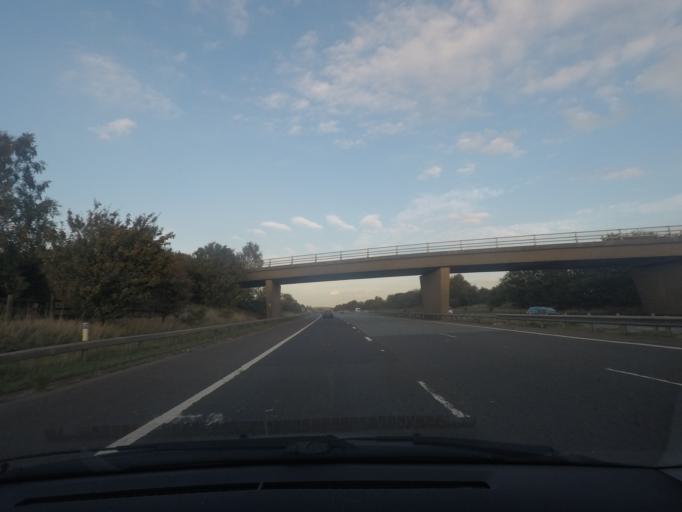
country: GB
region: England
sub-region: North Lincolnshire
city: Brigg
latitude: 53.5623
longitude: -0.4905
